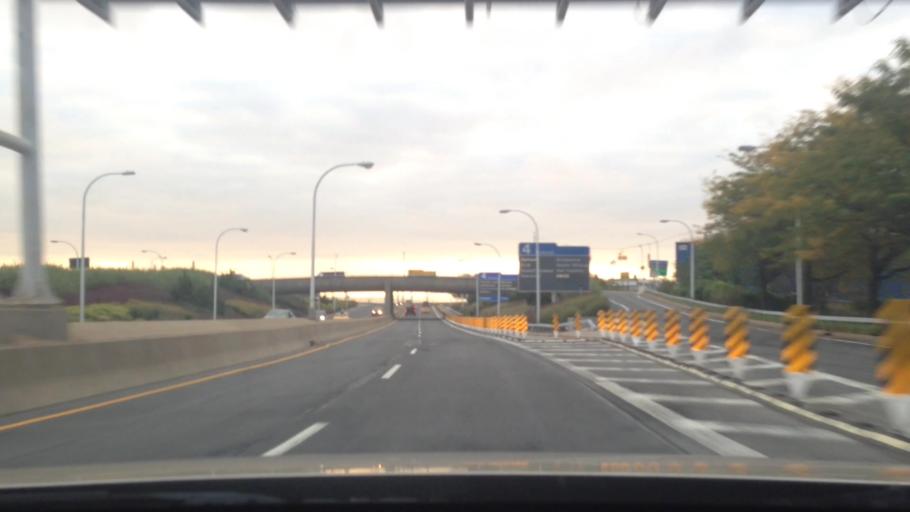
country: US
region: New York
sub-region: Queens County
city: Jamaica
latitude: 40.6557
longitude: -73.7914
